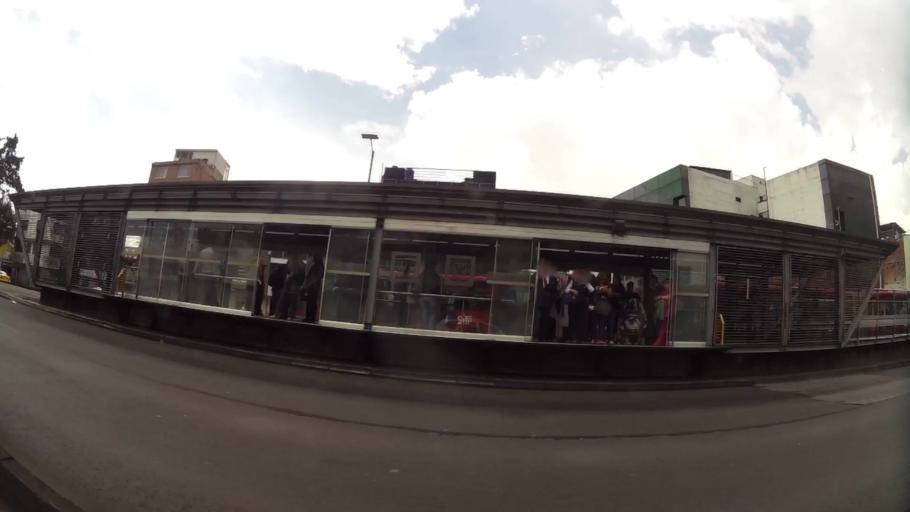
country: CO
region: Bogota D.C.
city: Bogota
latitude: 4.5828
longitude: -74.0996
